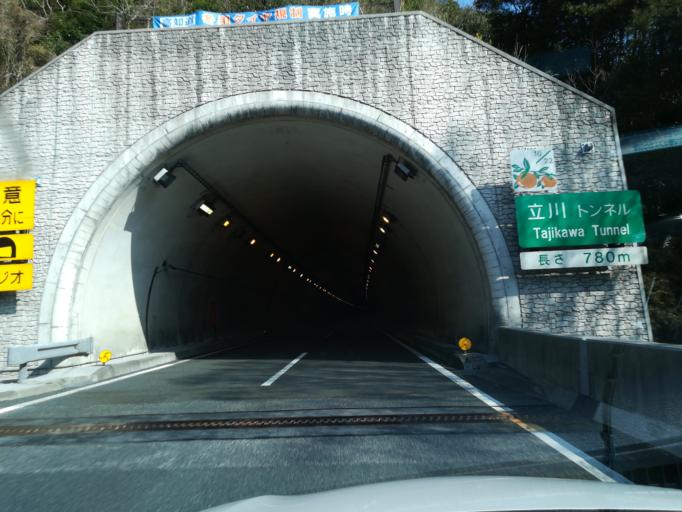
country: JP
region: Ehime
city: Kawanoecho
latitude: 33.8363
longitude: 133.6547
